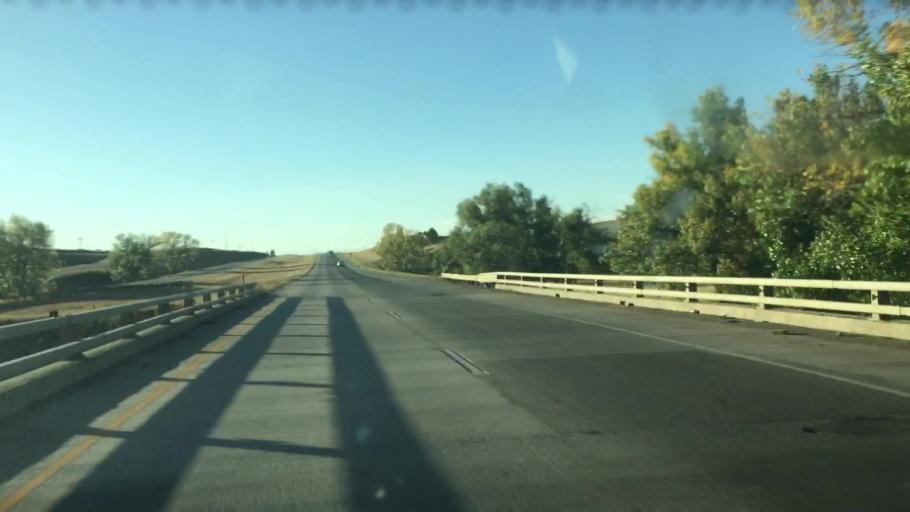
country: US
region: Colorado
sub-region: Arapahoe County
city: Byers
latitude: 39.6722
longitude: -104.0989
